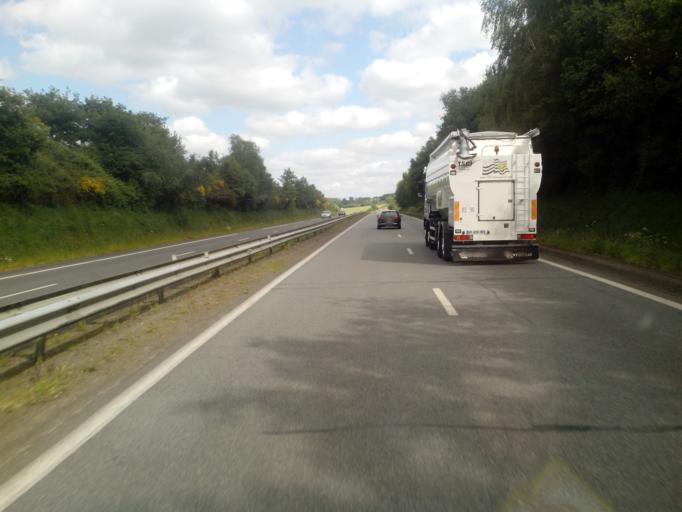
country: FR
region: Brittany
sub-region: Departement des Cotes-d'Armor
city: Broons
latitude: 48.2952
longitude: -2.2239
